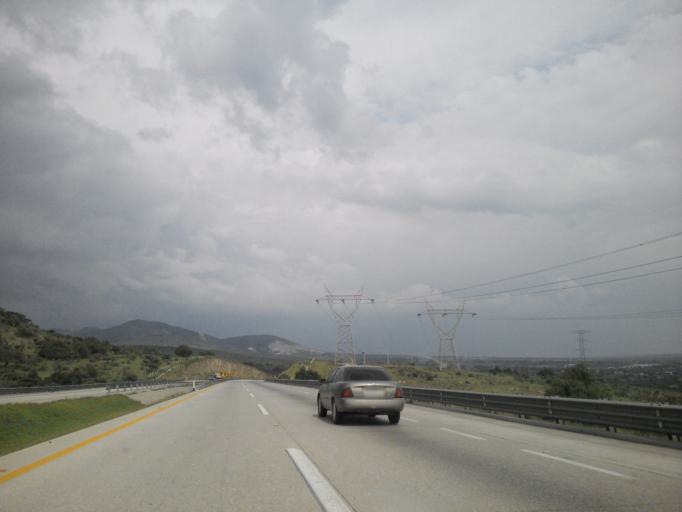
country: MX
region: Mexico
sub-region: Apaxco
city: Colonia Juarez
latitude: 20.0160
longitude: -99.1569
